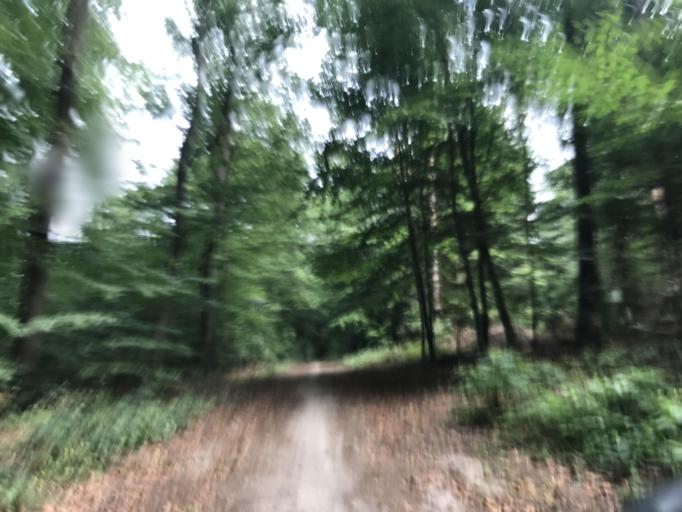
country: DE
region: Lower Saxony
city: Vastorf
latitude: 53.2158
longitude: 10.5378
